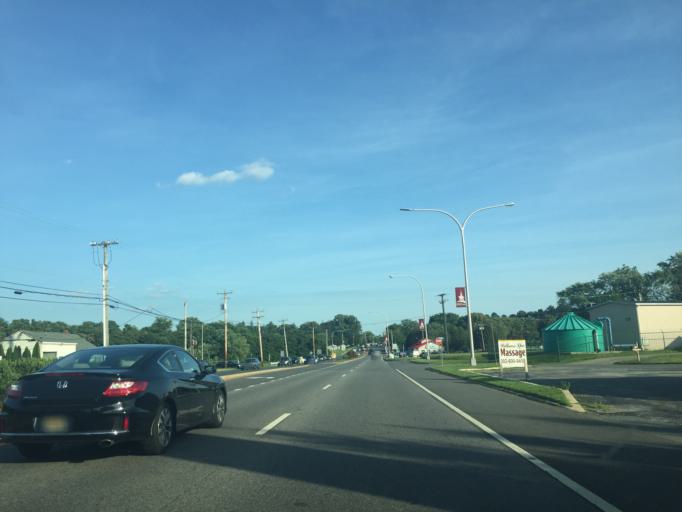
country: US
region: Delaware
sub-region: Kent County
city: Smyrna
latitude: 39.2985
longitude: -75.6009
